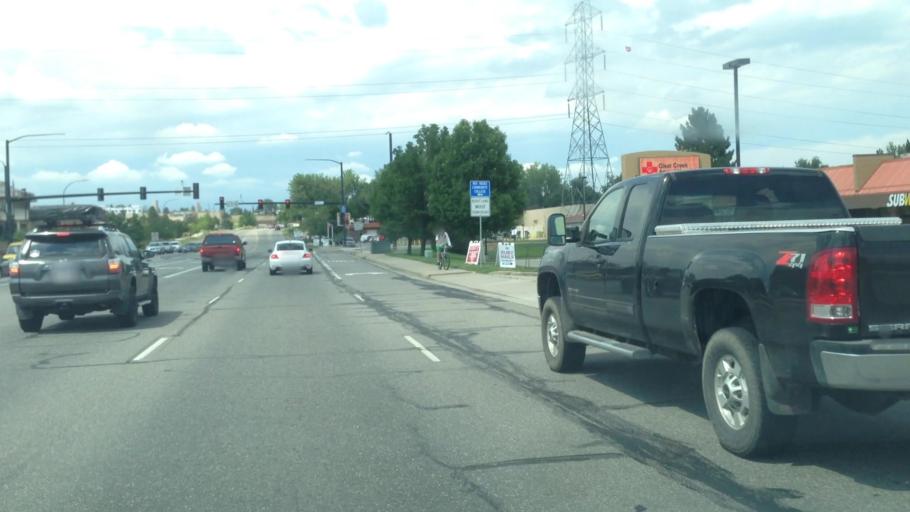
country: US
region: Colorado
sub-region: Jefferson County
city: Arvada
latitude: 39.7863
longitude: -105.1095
